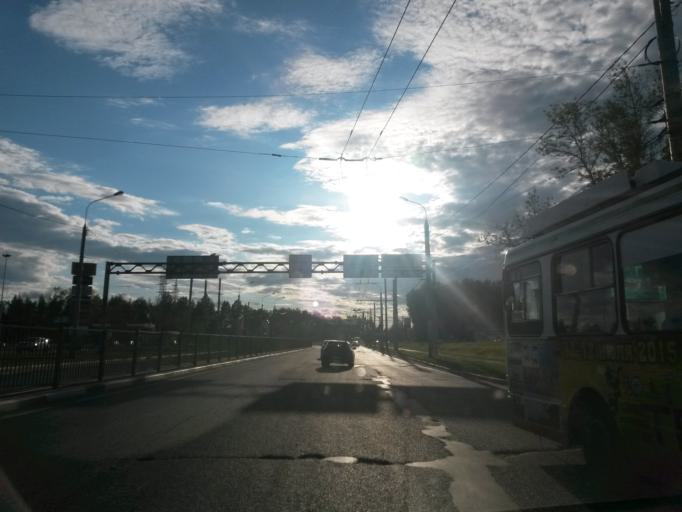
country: RU
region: Jaroslavl
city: Yaroslavl
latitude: 57.6720
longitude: 39.8368
